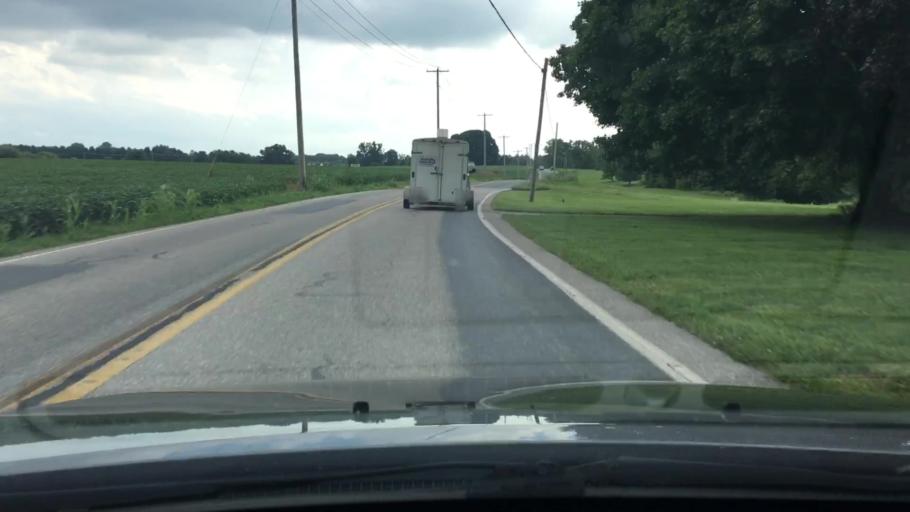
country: US
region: Pennsylvania
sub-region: Franklin County
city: Scotland
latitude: 39.9607
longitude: -77.5834
